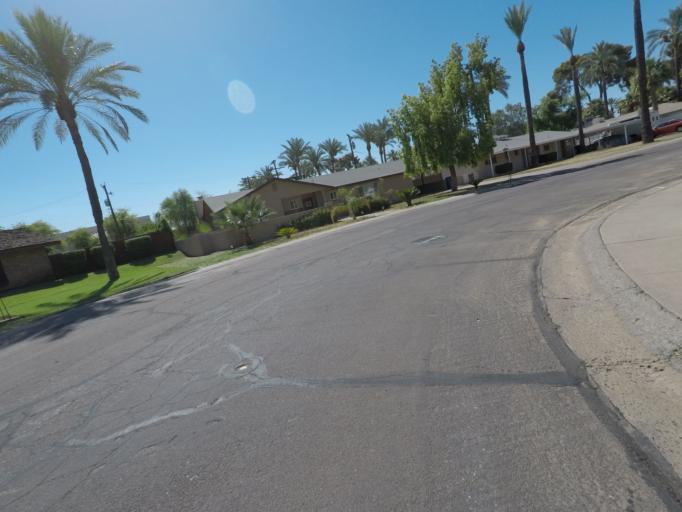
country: US
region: Arizona
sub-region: Maricopa County
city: Tempe Junction
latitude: 33.4066
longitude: -111.9414
